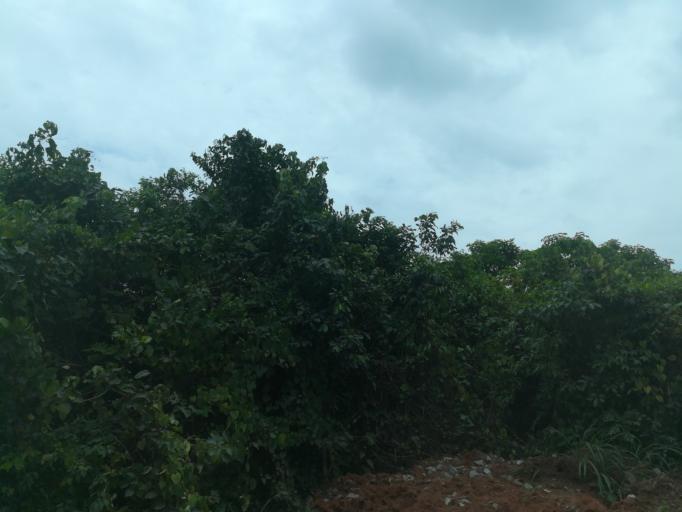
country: NG
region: Lagos
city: Ejirin
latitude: 6.6457
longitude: 3.8444
